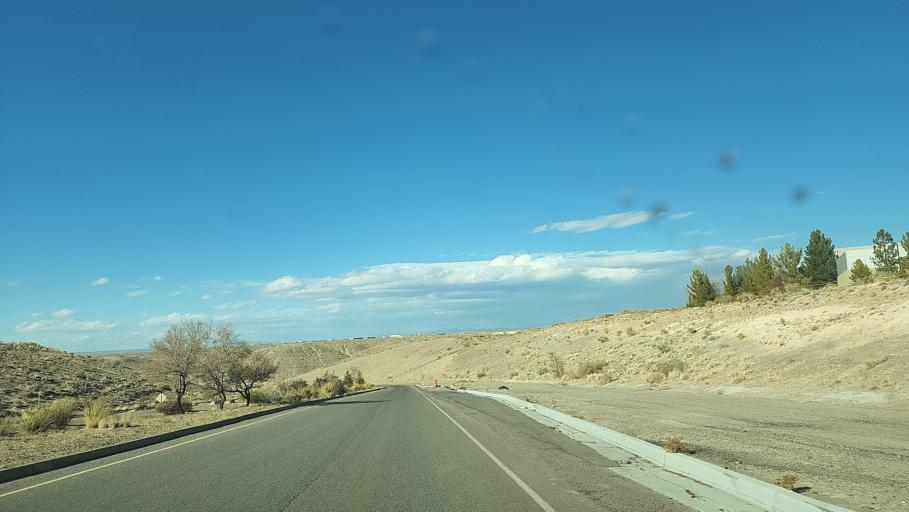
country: US
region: New Mexico
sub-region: Bernalillo County
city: South Valley
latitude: 35.0021
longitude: -106.6218
